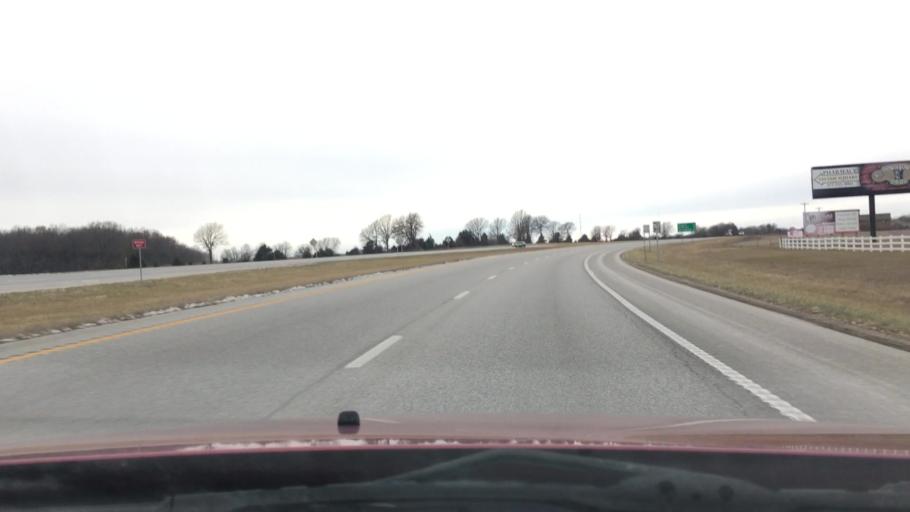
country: US
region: Missouri
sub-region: Webster County
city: Seymour
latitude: 37.1571
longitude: -92.7869
